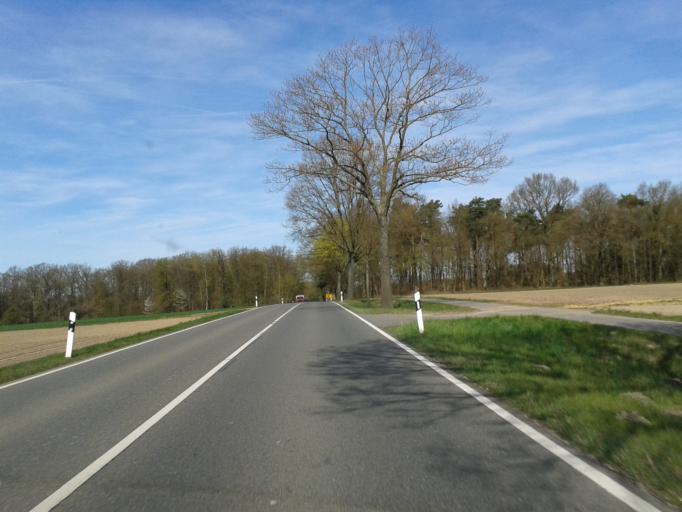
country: DE
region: Lower Saxony
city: Schwienau
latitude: 52.9585
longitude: 10.4703
